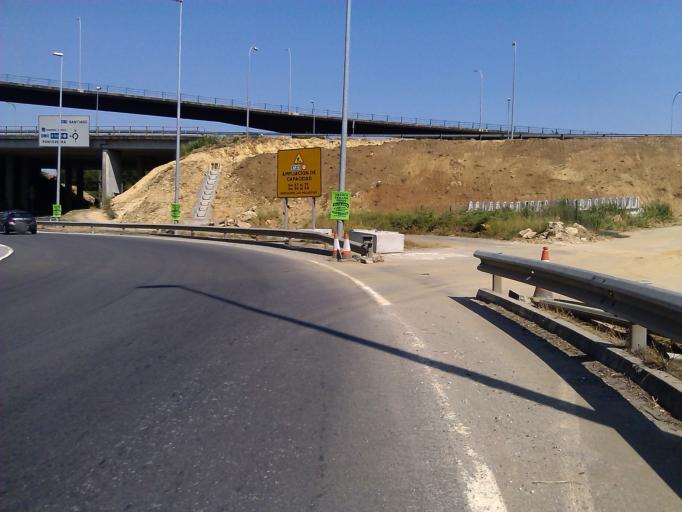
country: ES
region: Galicia
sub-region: Provincia da Coruna
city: Santiago de Compostela
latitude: 42.8554
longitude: -8.5307
